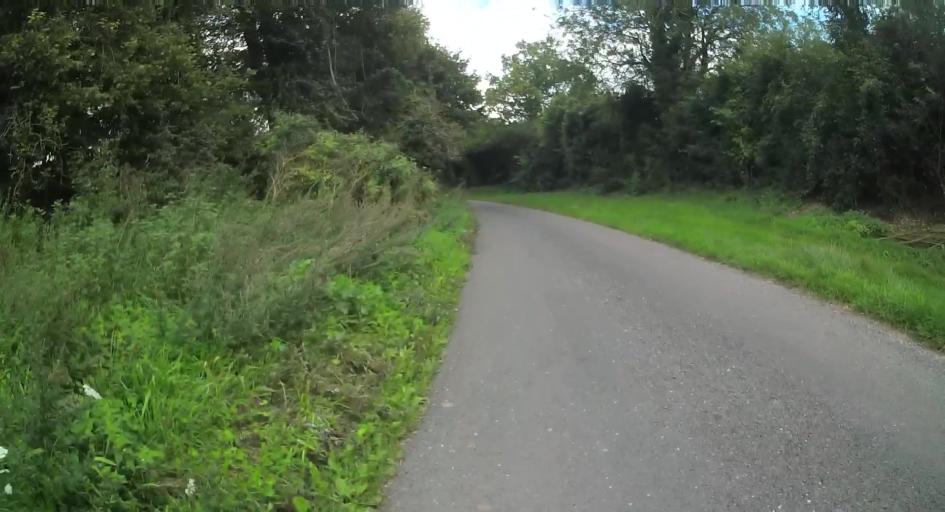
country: GB
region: England
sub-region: Hampshire
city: Overton
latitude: 51.2433
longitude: -1.3233
